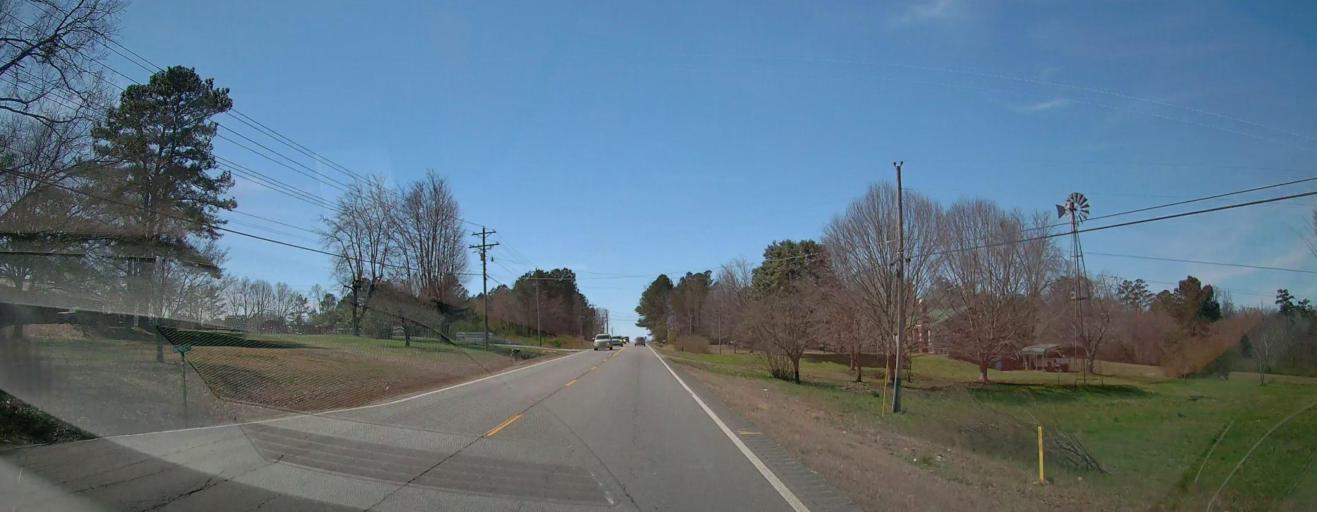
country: US
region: Alabama
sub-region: Blount County
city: Blountsville
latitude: 34.1747
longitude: -86.6332
